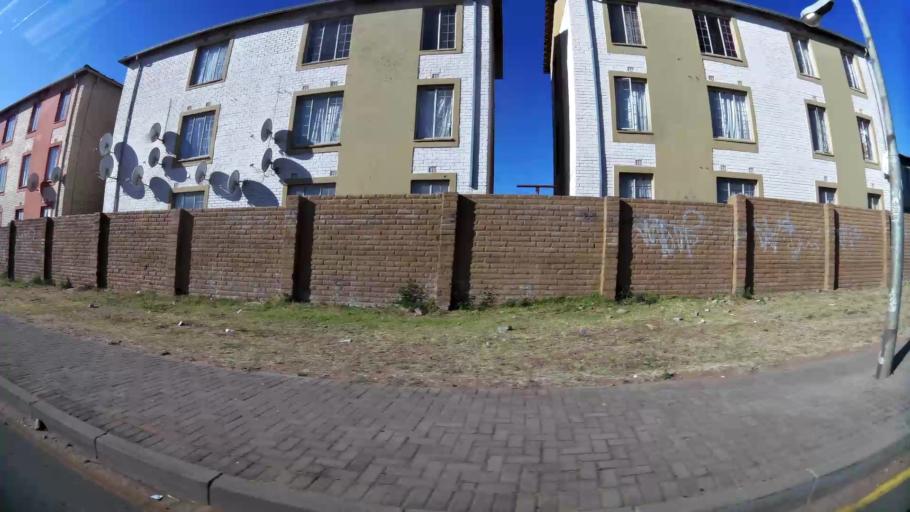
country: ZA
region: Gauteng
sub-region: City of Johannesburg Metropolitan Municipality
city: Roodepoort
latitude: -26.2151
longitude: 27.9470
